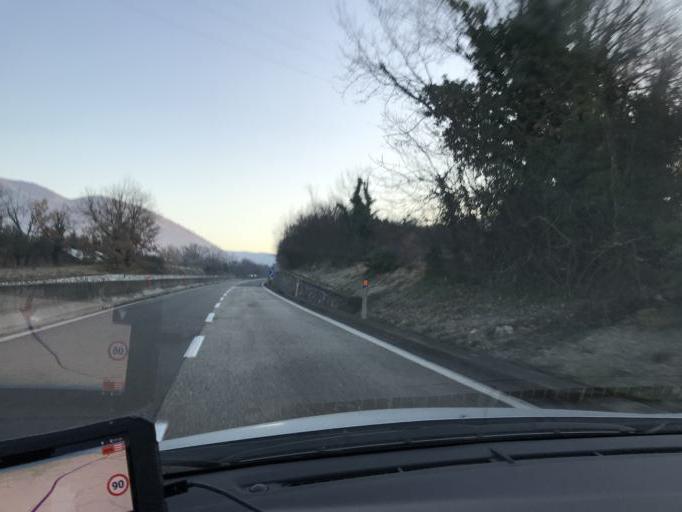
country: IT
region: Umbria
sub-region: Provincia di Terni
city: Terni
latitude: 42.5832
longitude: 12.6425
